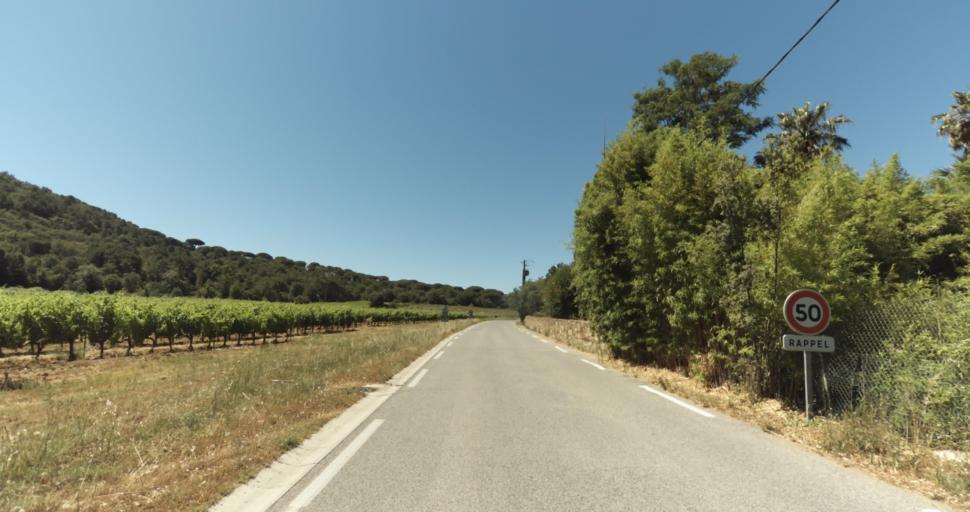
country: FR
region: Provence-Alpes-Cote d'Azur
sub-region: Departement du Var
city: Gassin
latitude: 43.2468
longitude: 6.5781
